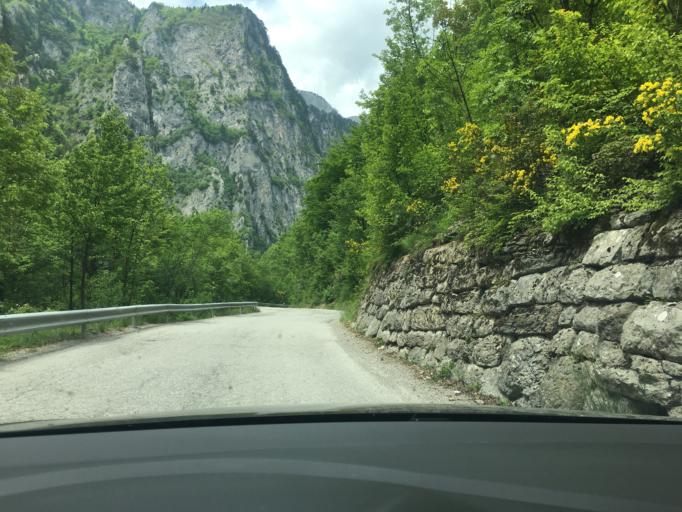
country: XK
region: Pec
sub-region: Komuna e Pejes
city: Peje
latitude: 42.6628
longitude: 20.2153
